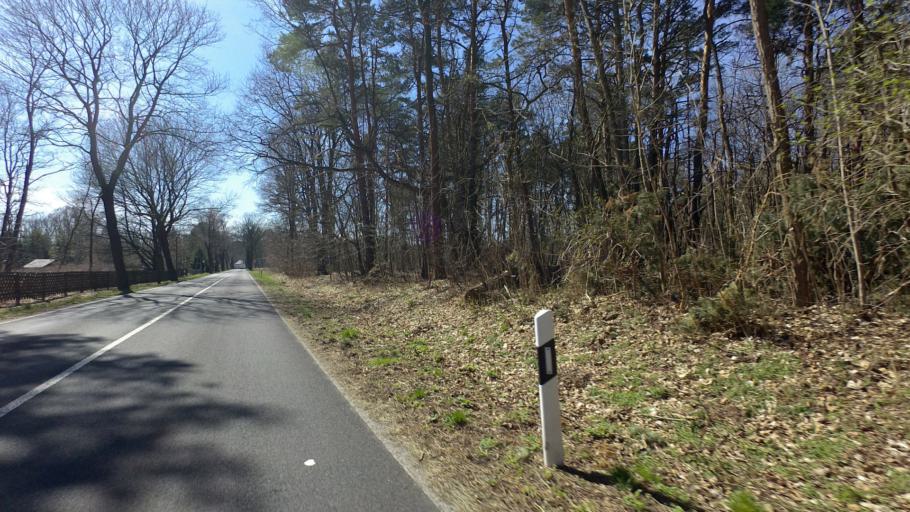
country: DE
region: Brandenburg
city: Teupitz
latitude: 52.1418
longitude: 13.5863
